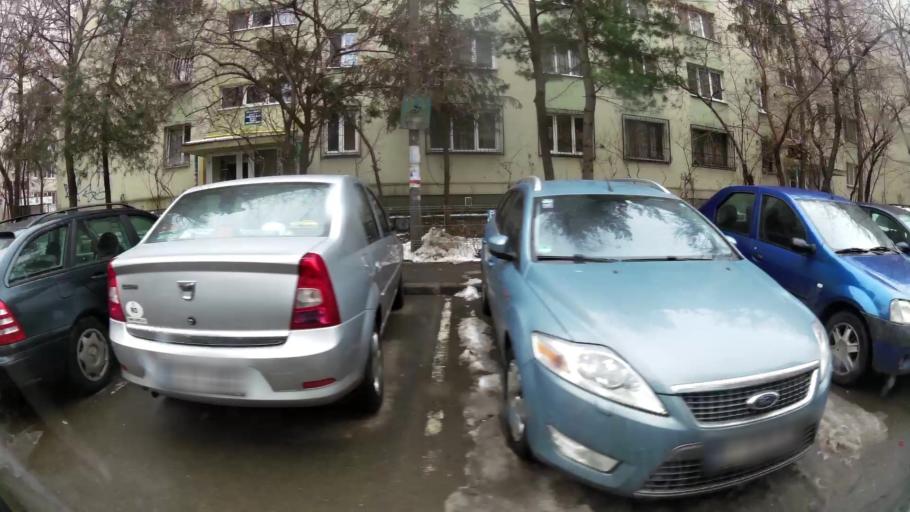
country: RO
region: Ilfov
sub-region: Comuna Chiajna
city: Rosu
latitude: 44.4185
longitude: 26.0240
